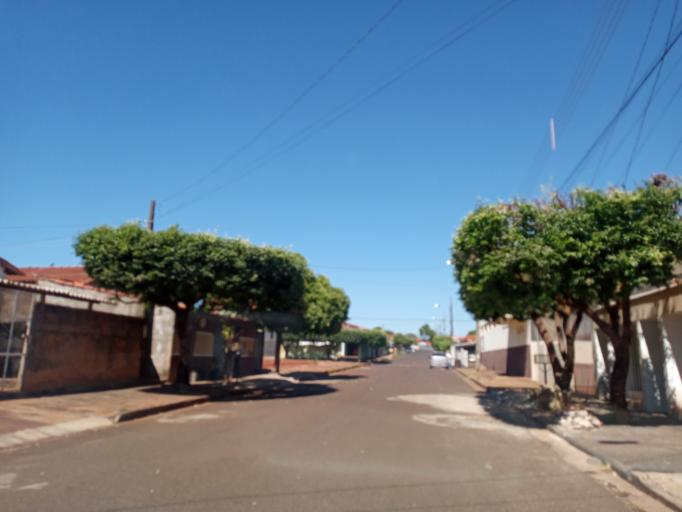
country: BR
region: Minas Gerais
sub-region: Ituiutaba
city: Ituiutaba
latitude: -18.9805
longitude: -49.4890
